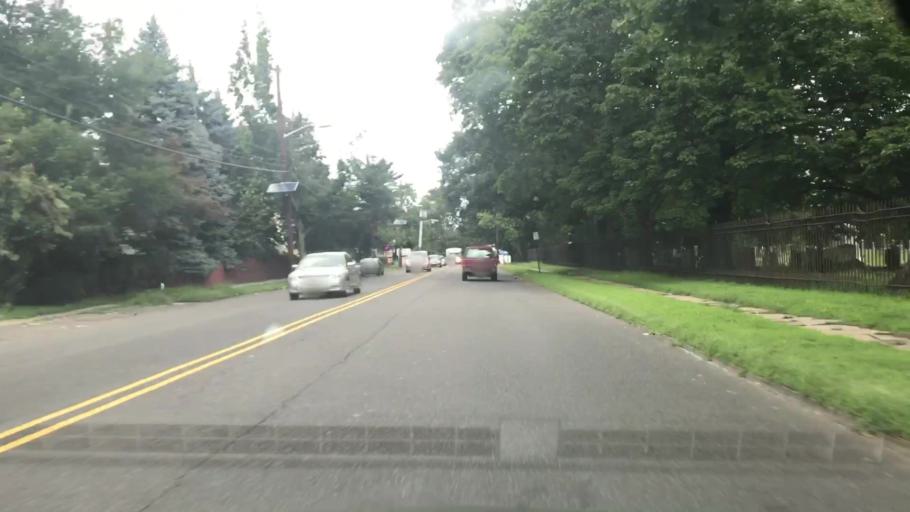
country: US
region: New Jersey
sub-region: Union County
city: Hillside
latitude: 40.6921
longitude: -74.2156
